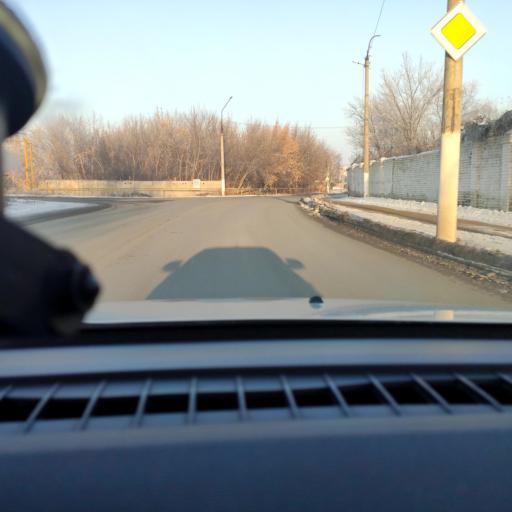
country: RU
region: Samara
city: Chapayevsk
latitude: 52.9684
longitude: 49.6953
